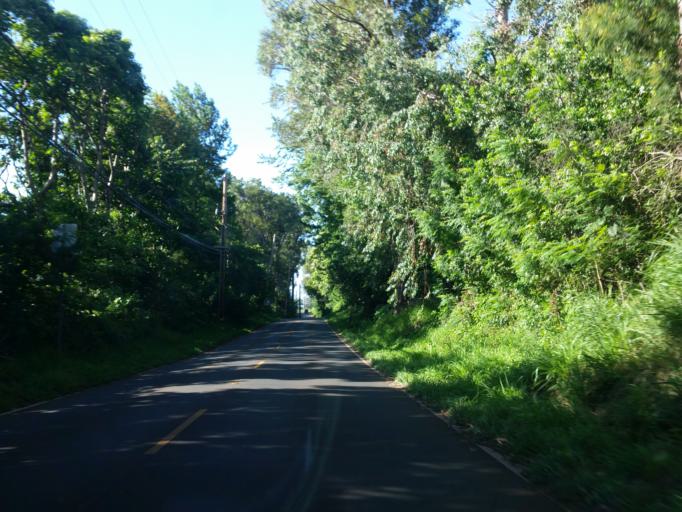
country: US
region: Hawaii
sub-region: Maui County
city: Makawao
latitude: 20.8439
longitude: -156.3087
